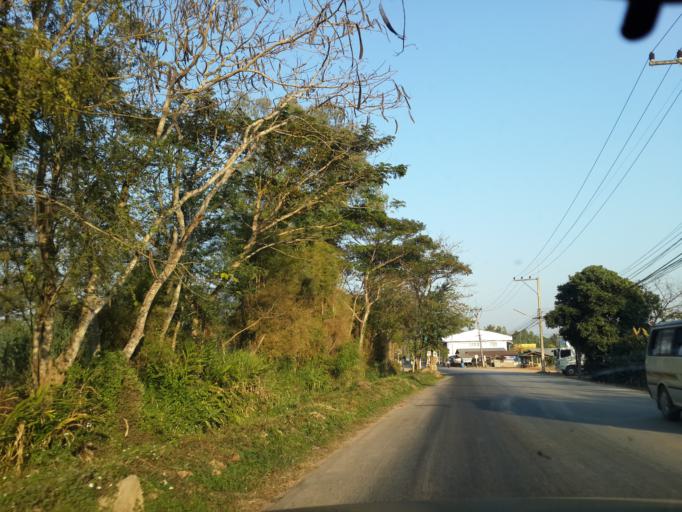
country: TH
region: Chiang Mai
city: Chai Prakan
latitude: 19.8023
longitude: 99.1655
